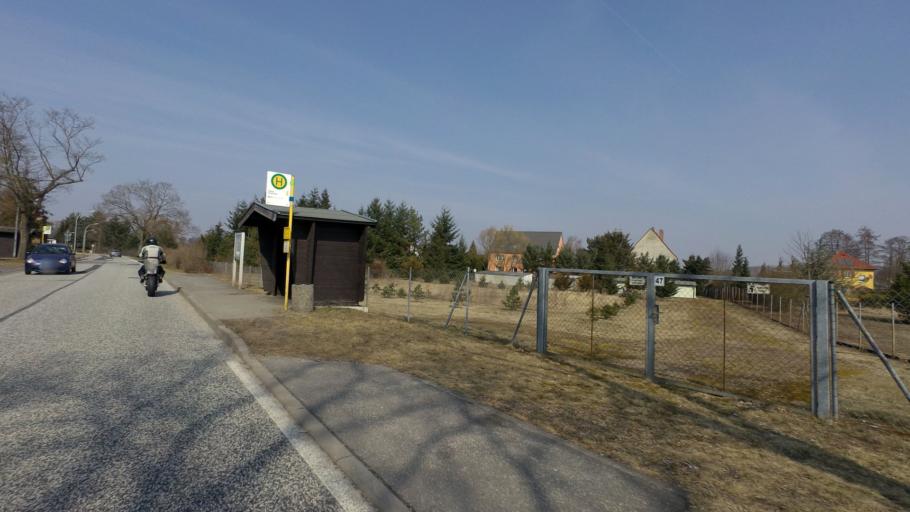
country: DE
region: Brandenburg
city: Werder
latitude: 52.4248
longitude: 12.8890
